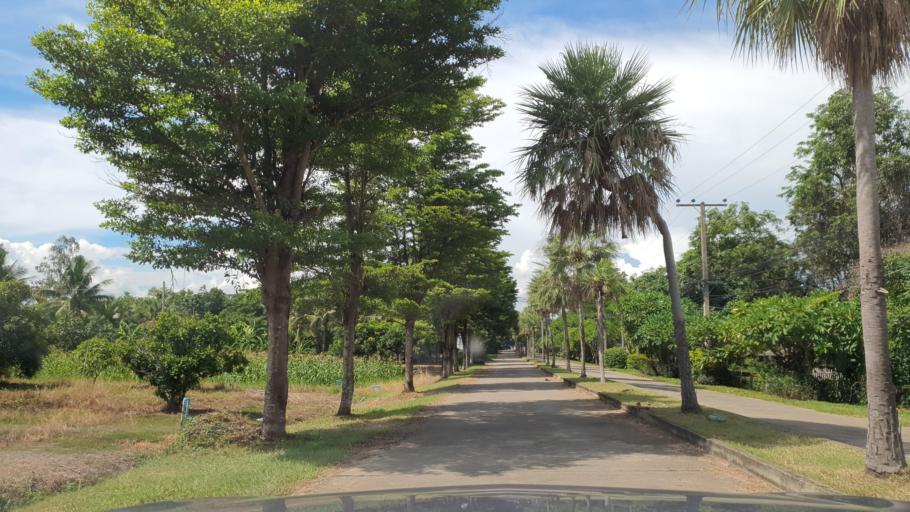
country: TH
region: Chiang Mai
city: San Pa Tong
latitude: 18.5912
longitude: 98.8751
